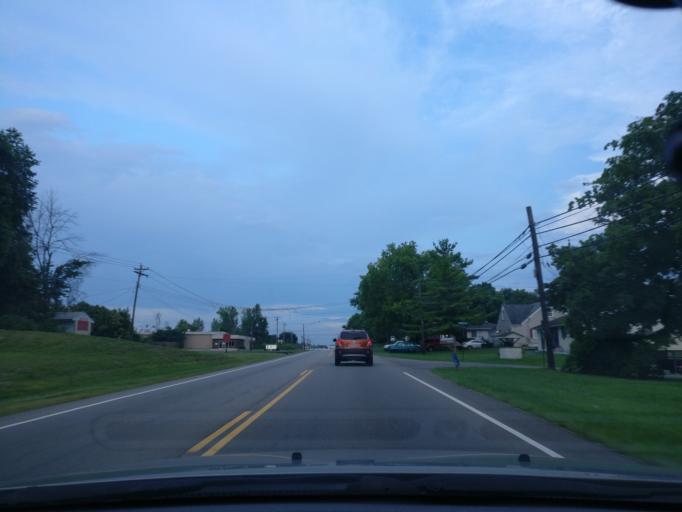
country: US
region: Ohio
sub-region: Warren County
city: Franklin
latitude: 39.5477
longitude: -84.2963
